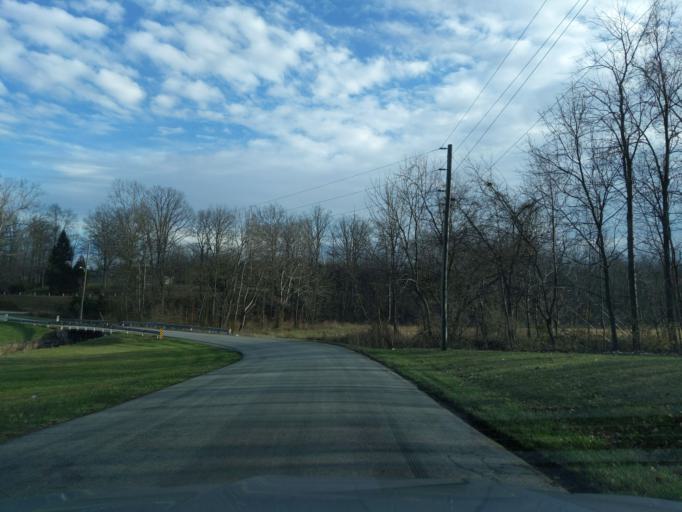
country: US
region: Indiana
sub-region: Decatur County
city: Greensburg
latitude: 39.2118
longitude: -85.4450
